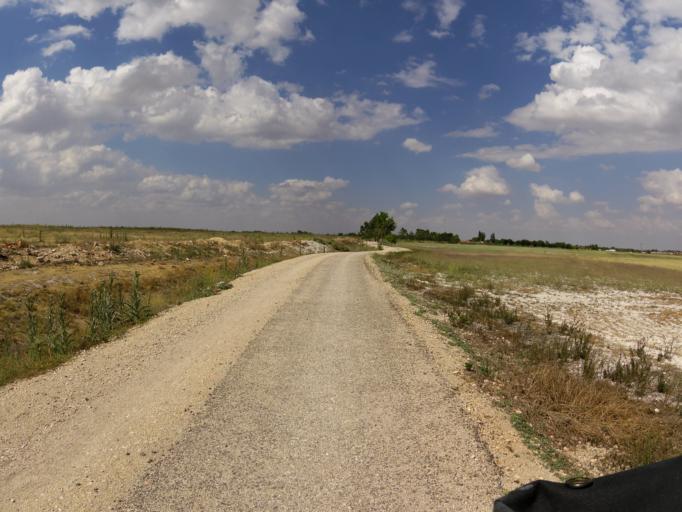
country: ES
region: Castille-La Mancha
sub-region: Provincia de Albacete
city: Albacete
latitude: 38.9686
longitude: -1.9382
